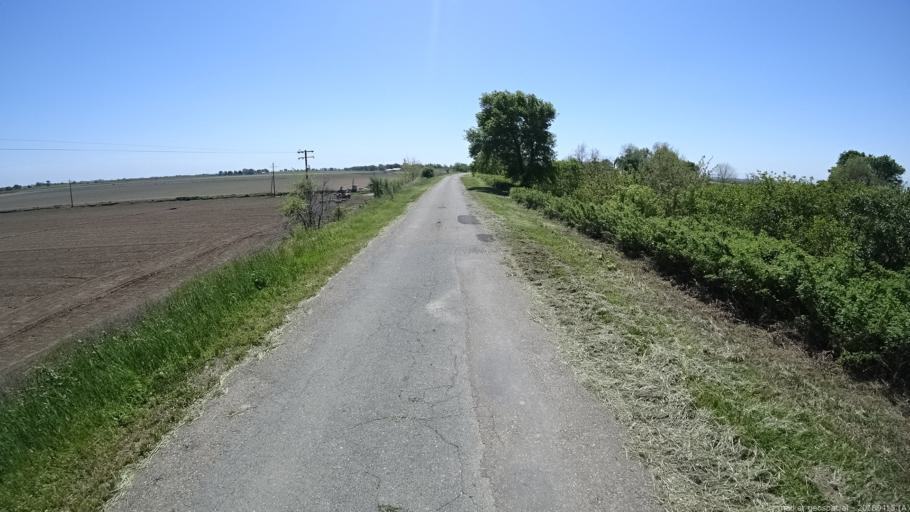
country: US
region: California
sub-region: Sacramento County
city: Walnut Grove
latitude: 38.2769
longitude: -121.6007
